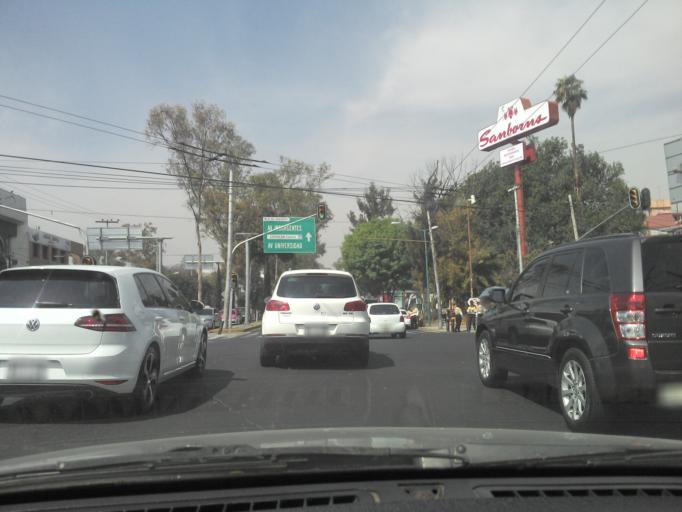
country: MX
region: Mexico City
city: Coyoacan
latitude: 19.3427
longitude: -99.1487
